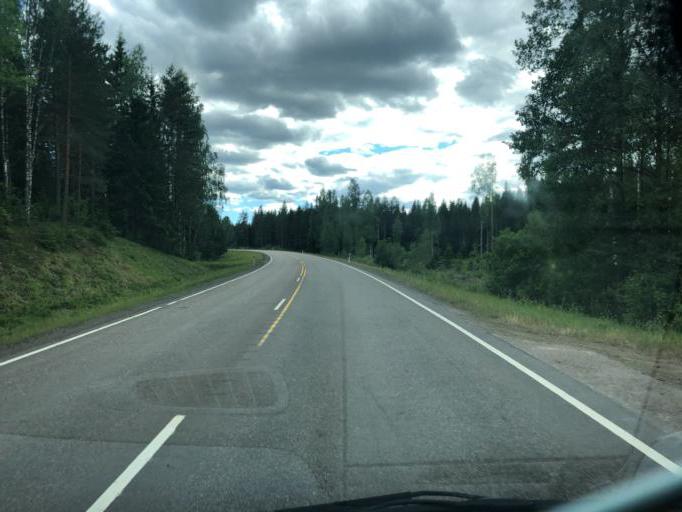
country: FI
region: Kymenlaakso
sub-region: Kouvola
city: Kouvola
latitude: 61.0400
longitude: 26.9934
